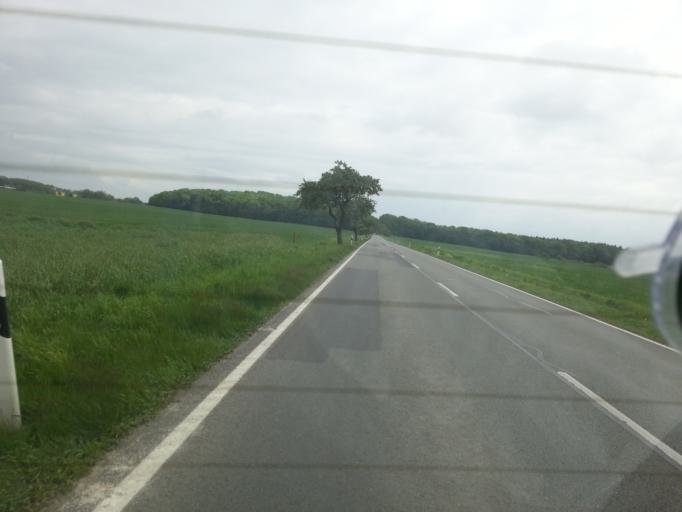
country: DE
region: Mecklenburg-Vorpommern
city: Klink
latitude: 53.4535
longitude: 12.5236
